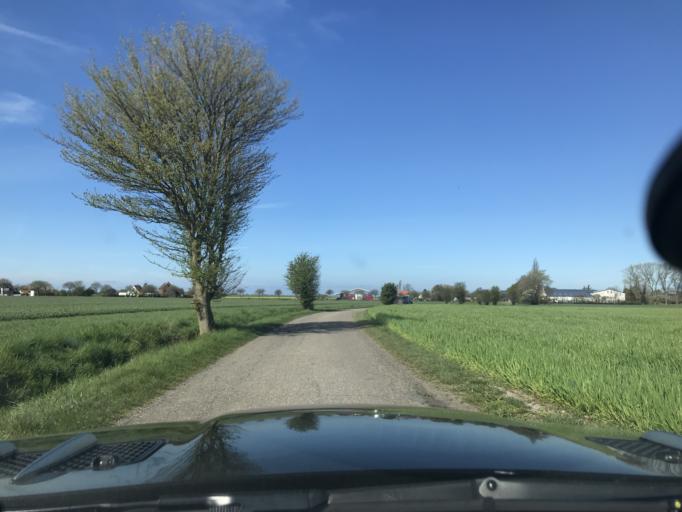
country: DE
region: Schleswig-Holstein
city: Grossenbrode
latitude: 54.4561
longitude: 11.0519
